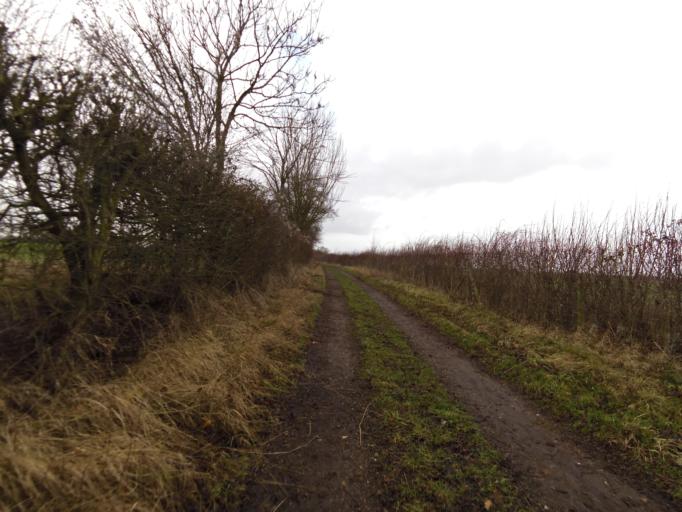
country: GB
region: England
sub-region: Suffolk
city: Needham Market
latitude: 52.1565
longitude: 1.0709
